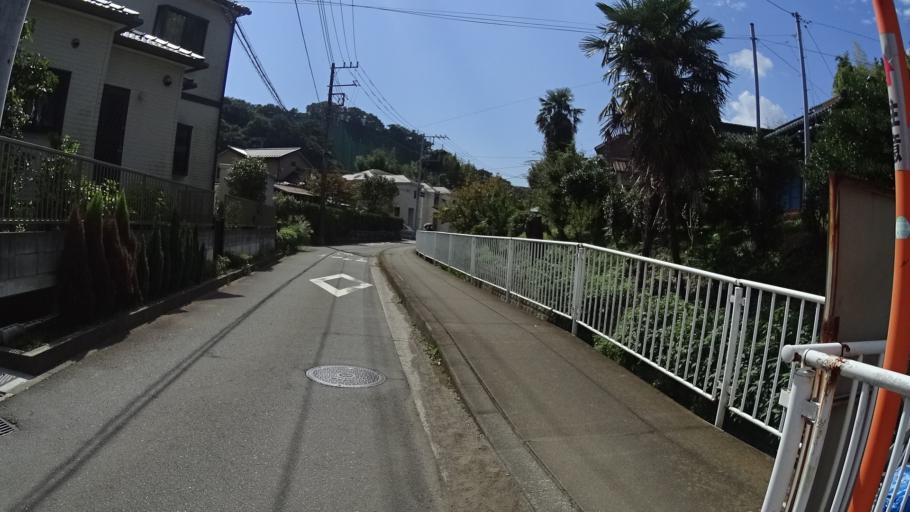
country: JP
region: Kanagawa
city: Zushi
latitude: 35.3612
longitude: 139.6061
